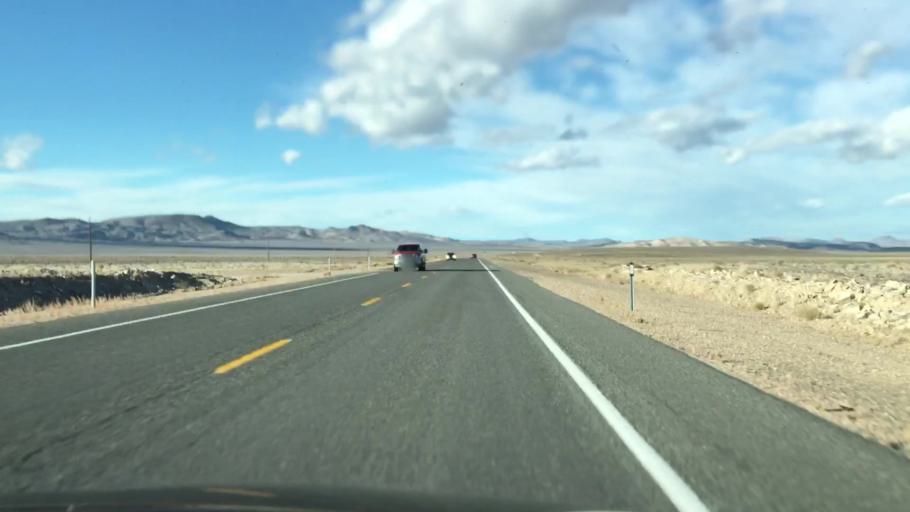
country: US
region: Nevada
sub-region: Esmeralda County
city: Goldfield
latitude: 37.4523
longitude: -117.1691
